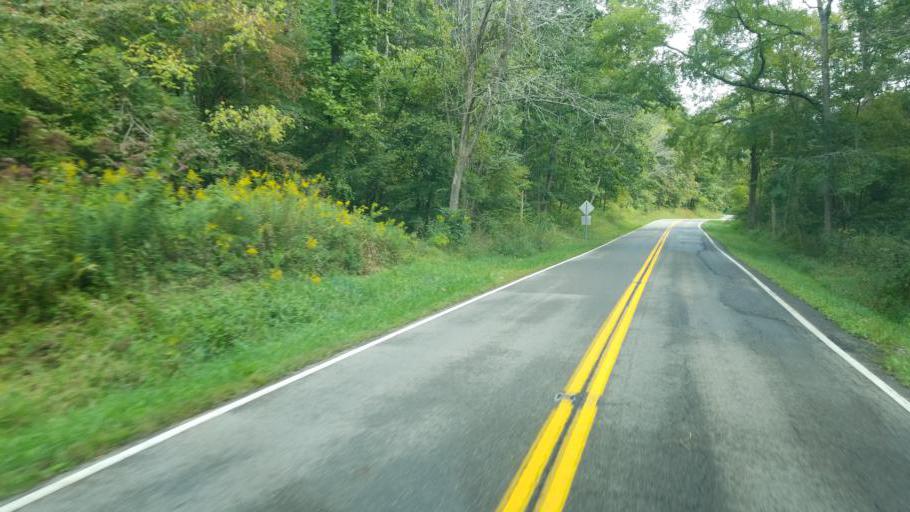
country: US
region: Ohio
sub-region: Jackson County
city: Oak Hill
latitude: 38.8842
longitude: -82.6745
